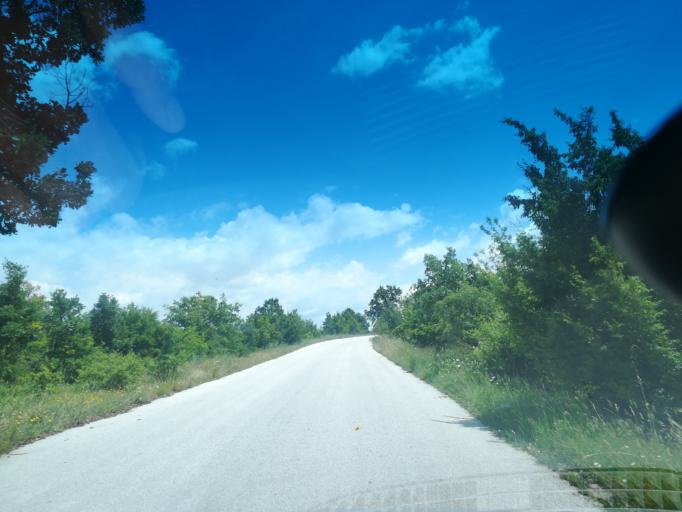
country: BG
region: Khaskovo
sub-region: Obshtina Mineralni Bani
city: Mineralni Bani
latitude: 41.9795
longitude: 25.2482
